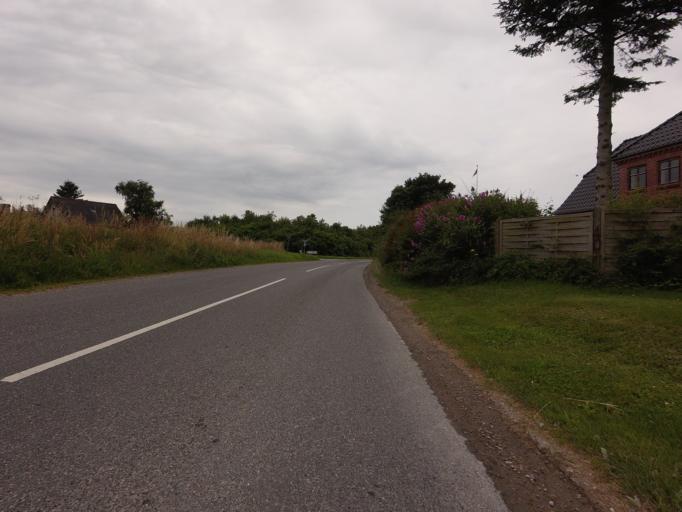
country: DK
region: North Denmark
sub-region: Alborg Kommune
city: Vadum
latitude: 57.1322
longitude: 9.8414
